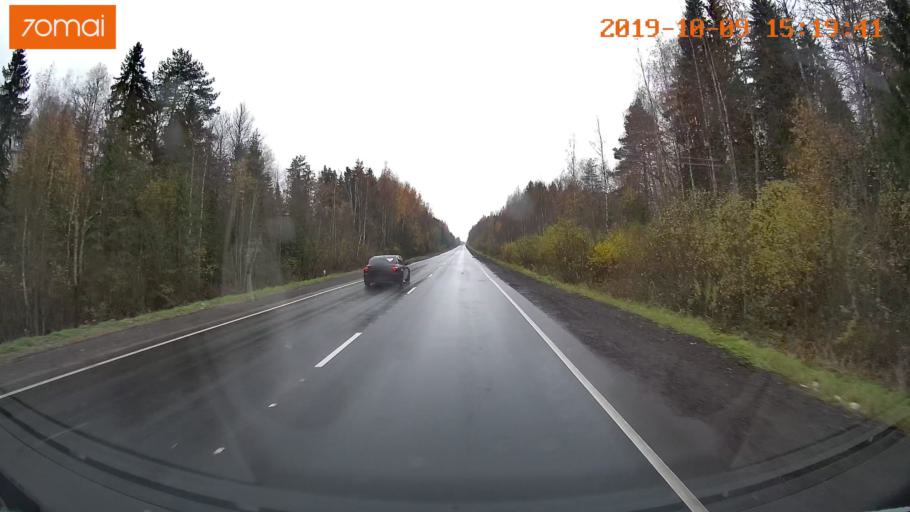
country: RU
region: Kostroma
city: Susanino
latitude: 58.0729
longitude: 41.5519
